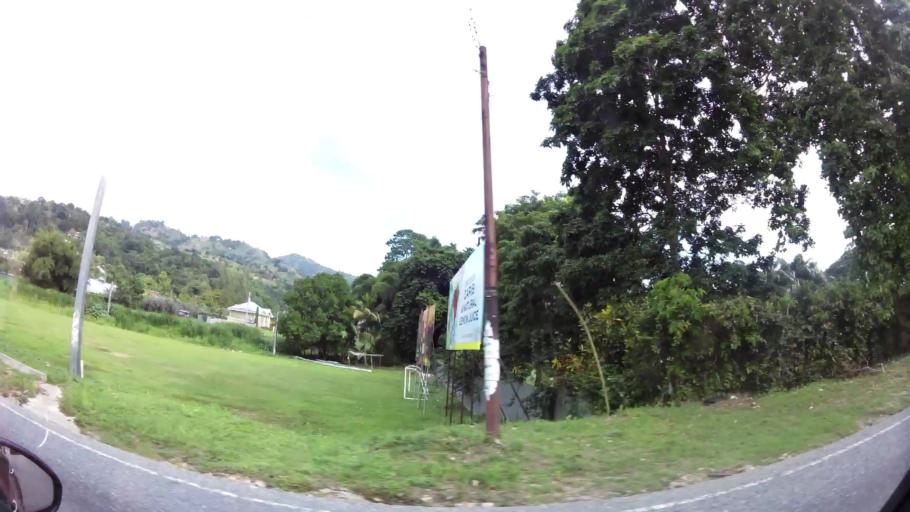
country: TT
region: Diego Martin
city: Petit Valley
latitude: 10.7132
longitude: -61.5046
